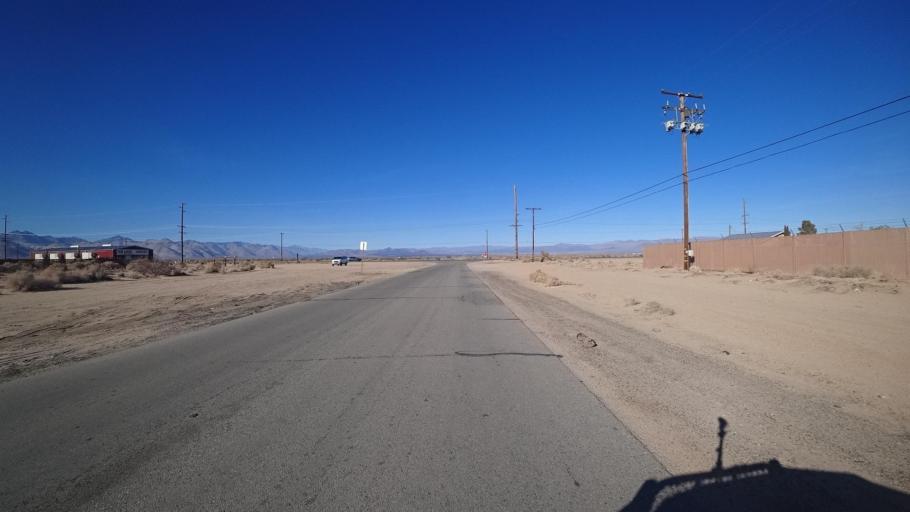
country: US
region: California
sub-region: Kern County
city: China Lake Acres
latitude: 35.6507
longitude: -117.7587
